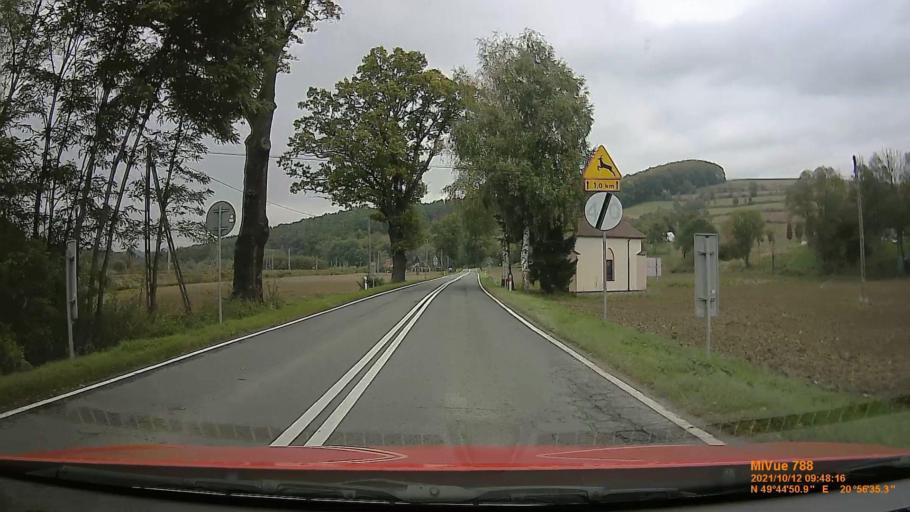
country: PL
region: Lesser Poland Voivodeship
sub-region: Powiat gorlicki
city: Bobowa
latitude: 49.7476
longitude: 20.9435
